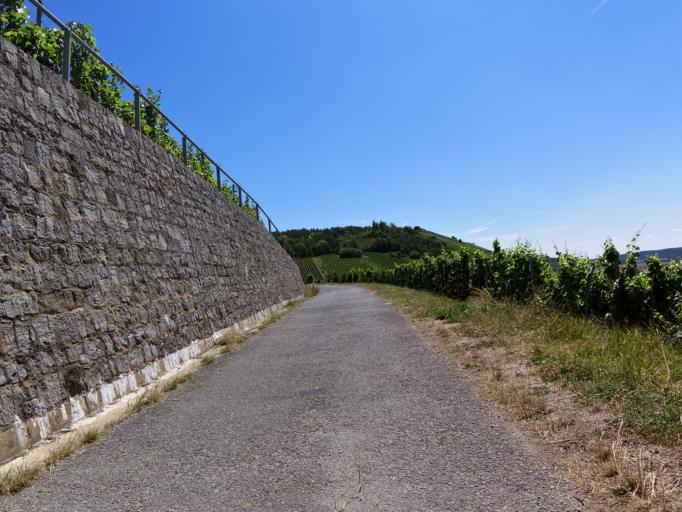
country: DE
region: Bavaria
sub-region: Regierungsbezirk Unterfranken
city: Randersacker
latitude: 49.7559
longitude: 9.9860
